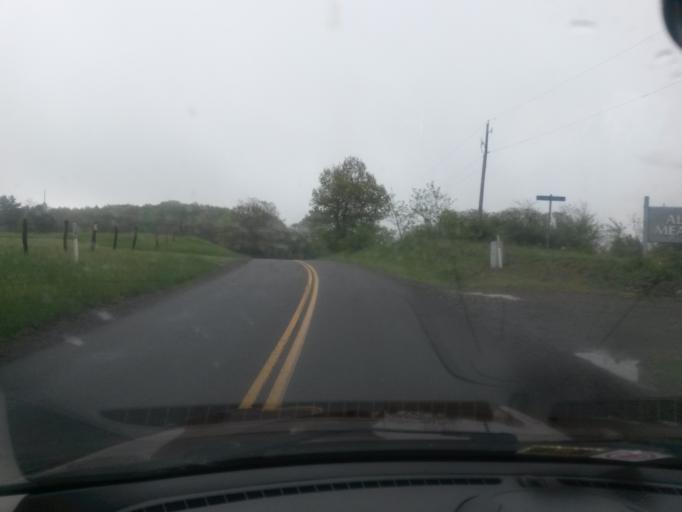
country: US
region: Virginia
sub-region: Floyd County
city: Floyd
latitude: 36.7931
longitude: -80.3876
